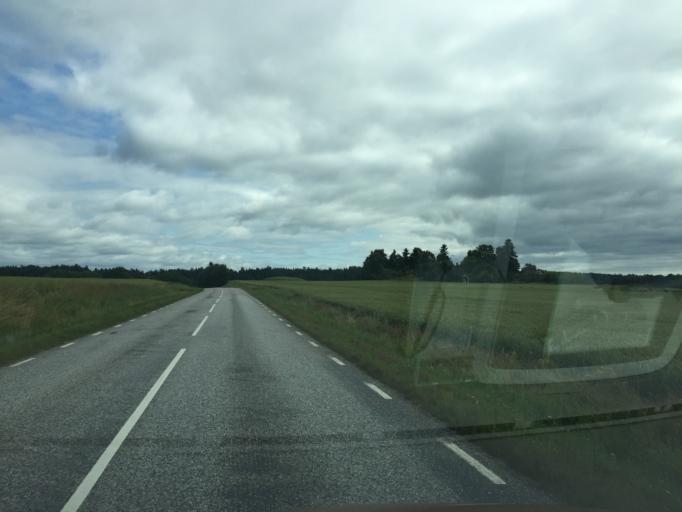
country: SE
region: Soedermanland
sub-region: Trosa Kommun
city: Vagnharad
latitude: 58.9911
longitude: 17.6467
